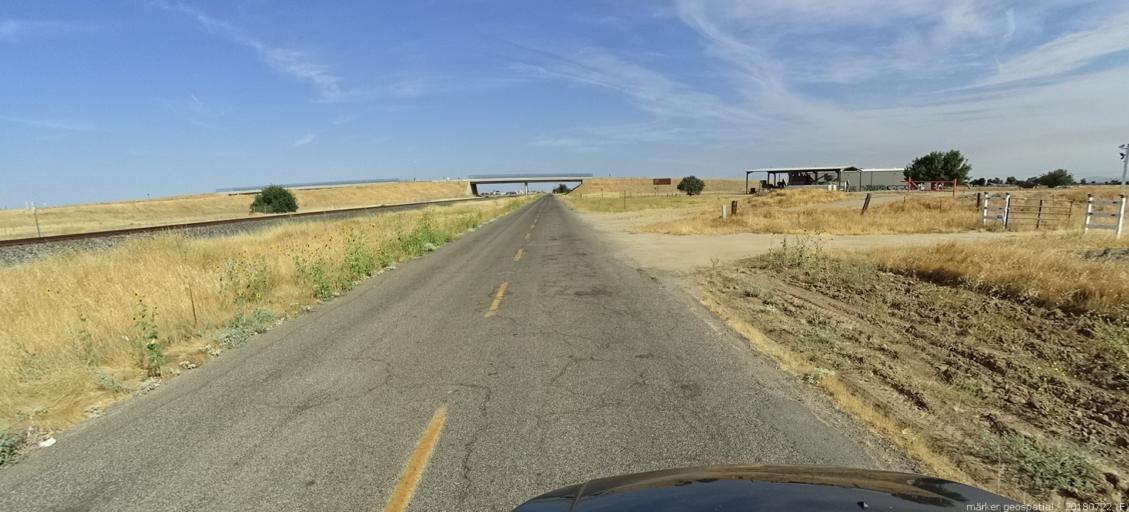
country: US
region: California
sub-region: Madera County
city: Fairmead
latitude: 37.0643
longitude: -120.1829
